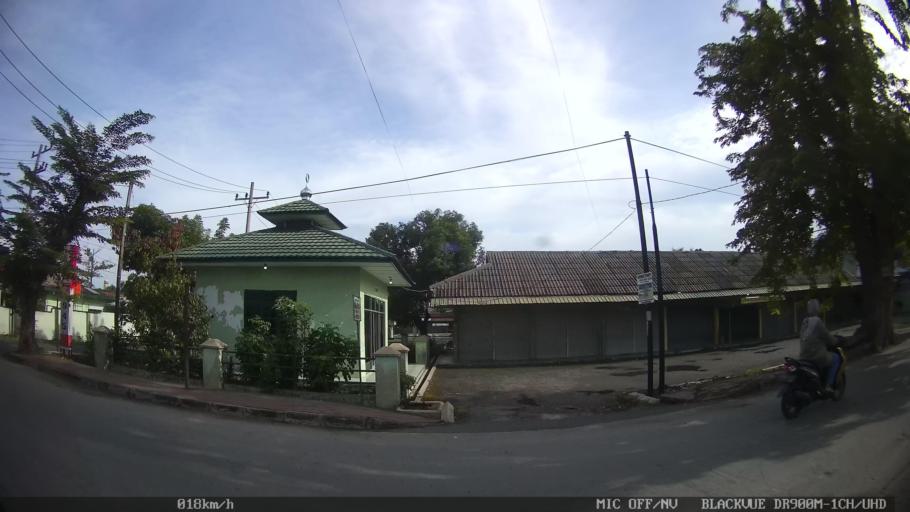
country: ID
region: North Sumatra
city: Medan
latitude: 3.6055
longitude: 98.6438
